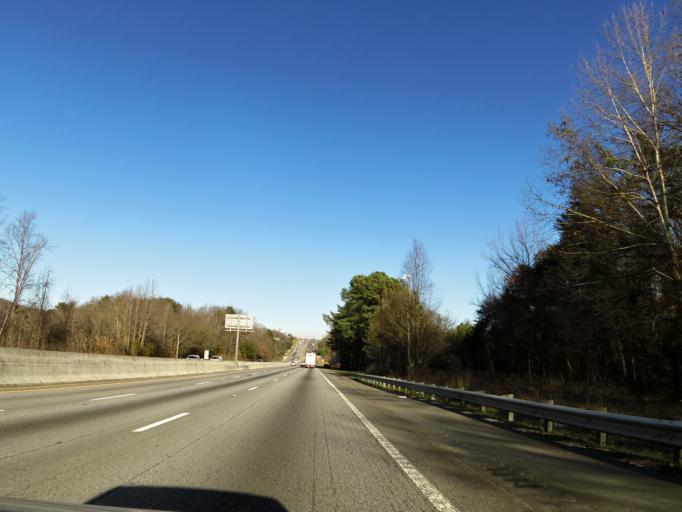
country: US
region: South Carolina
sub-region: Spartanburg County
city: Duncan
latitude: 34.9050
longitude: -82.1211
